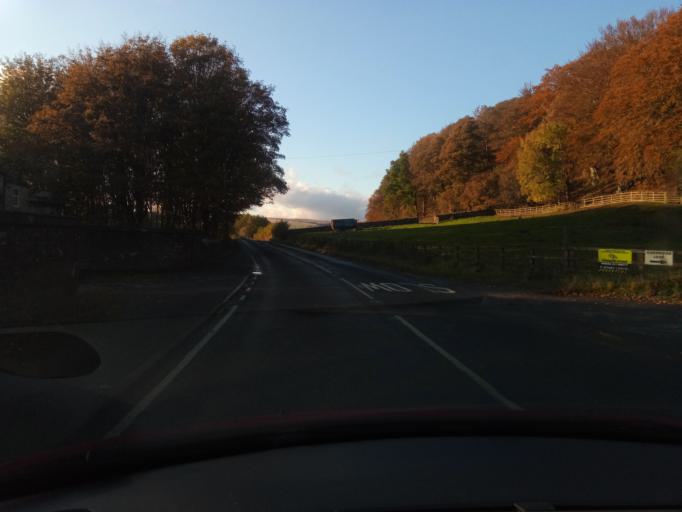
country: GB
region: England
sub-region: County Durham
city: Stanhope
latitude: 54.7332
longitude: -1.9786
